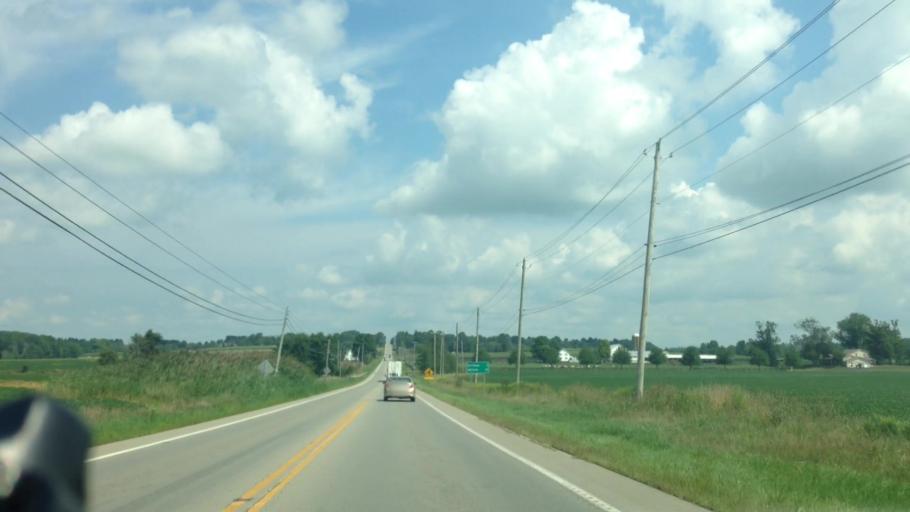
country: US
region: Ohio
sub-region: Wayne County
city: Orrville
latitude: 40.8700
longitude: -81.7634
